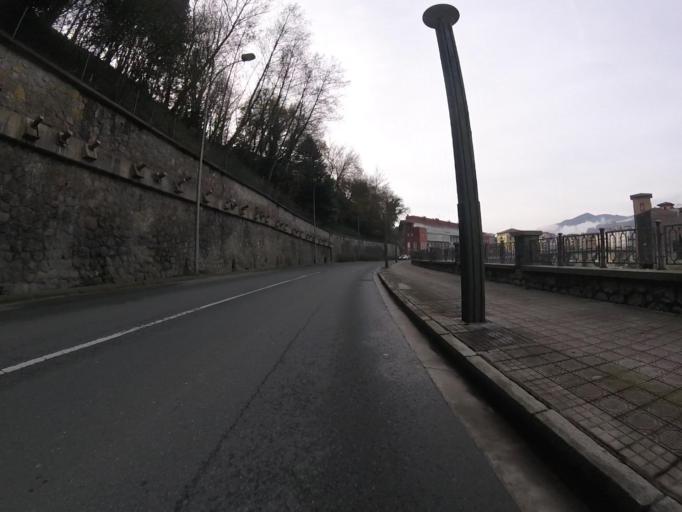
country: ES
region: Basque Country
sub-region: Provincia de Guipuzcoa
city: Ibarra
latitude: 43.1380
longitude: -2.0700
